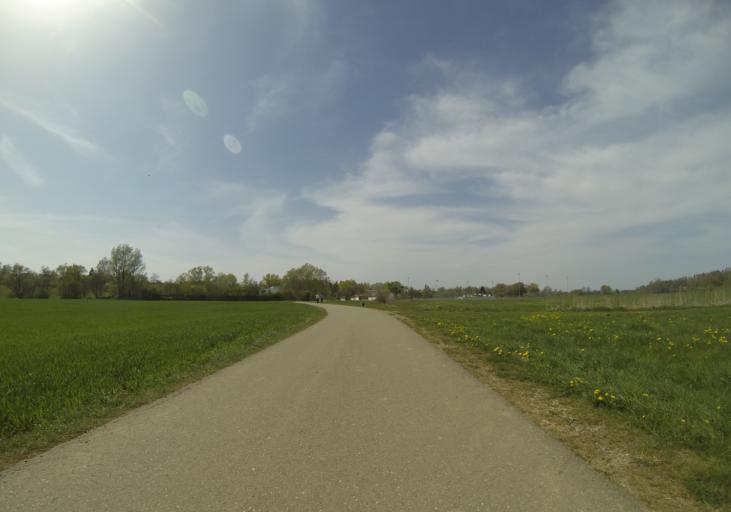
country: DE
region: Baden-Wuerttemberg
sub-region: Tuebingen Region
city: Achstetten
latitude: 48.2468
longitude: 9.9143
